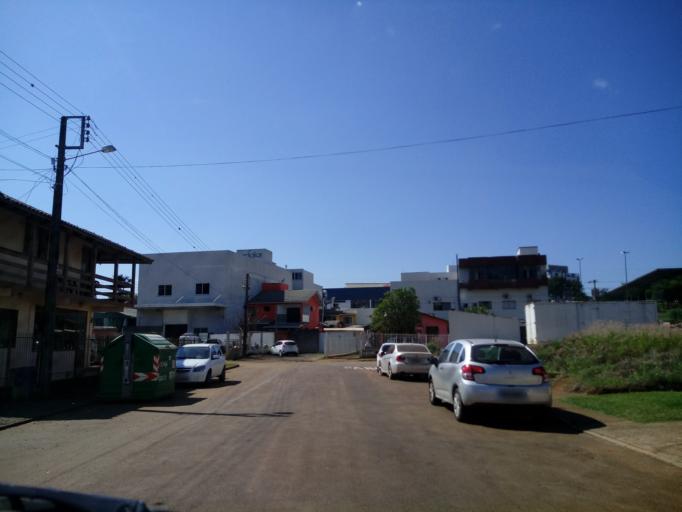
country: BR
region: Santa Catarina
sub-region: Chapeco
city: Chapeco
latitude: -27.0872
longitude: -52.6160
